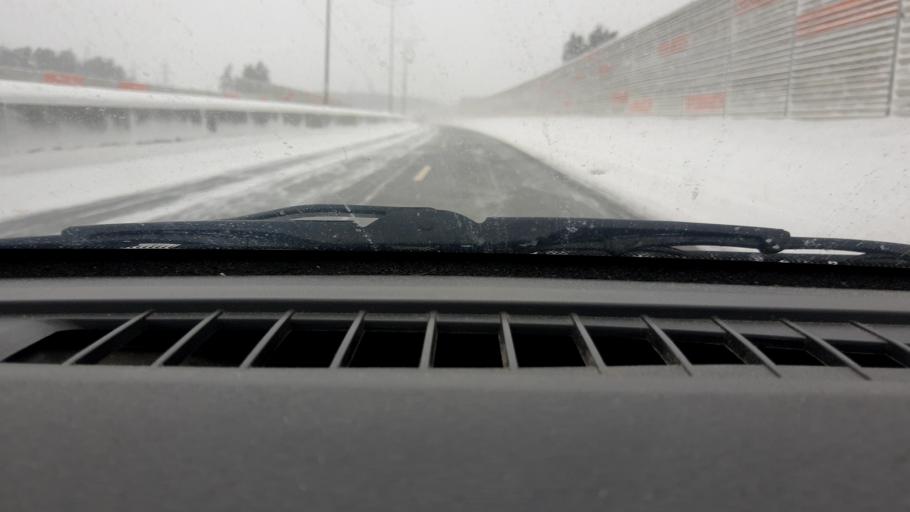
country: RU
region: Moskovskaya
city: Krasnoarmeysk
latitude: 56.0378
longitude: 38.2022
